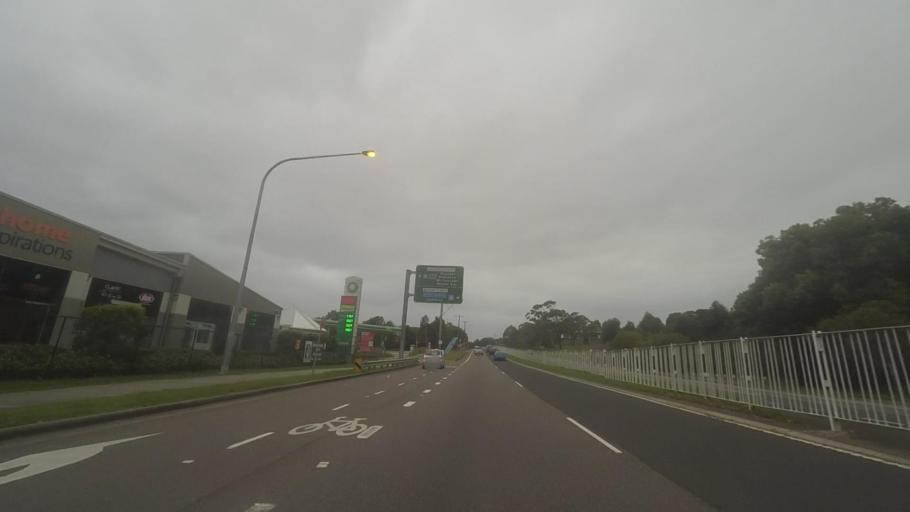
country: AU
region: New South Wales
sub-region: Newcastle
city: Mayfield West
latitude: -32.8849
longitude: 151.7257
